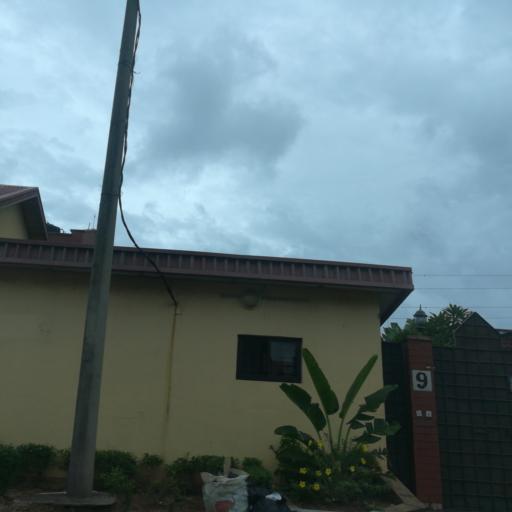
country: NG
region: Lagos
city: Ikoyi
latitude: 6.4477
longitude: 3.4555
